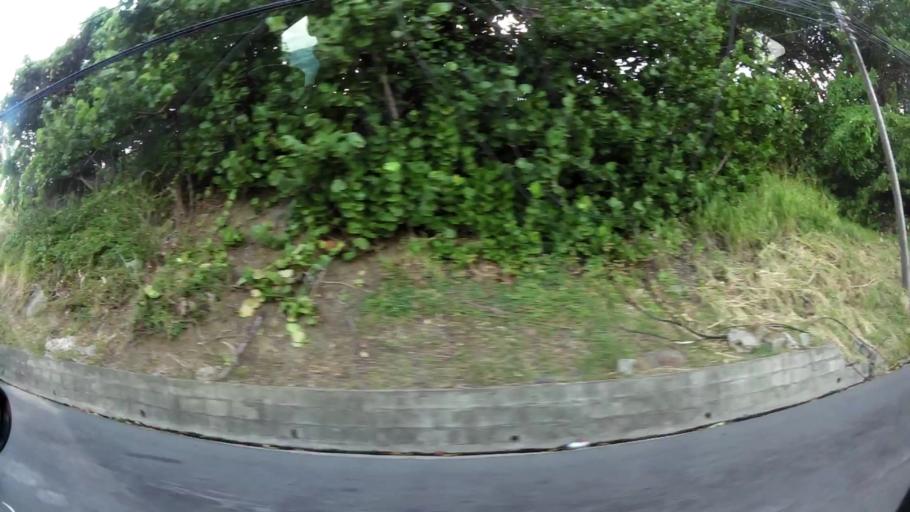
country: TT
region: Tobago
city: Scarborough
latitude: 11.1864
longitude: -60.6983
